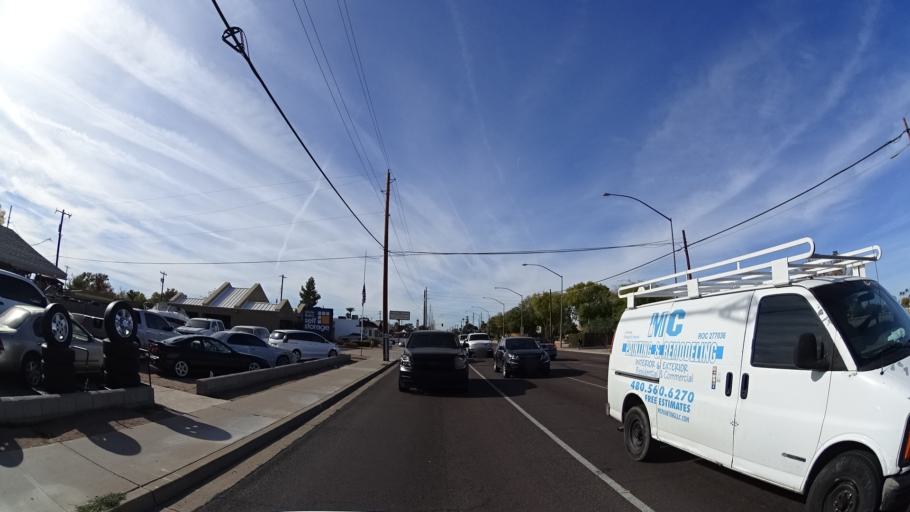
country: US
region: Arizona
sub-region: Maricopa County
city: Mesa
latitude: 33.4078
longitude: -111.8121
